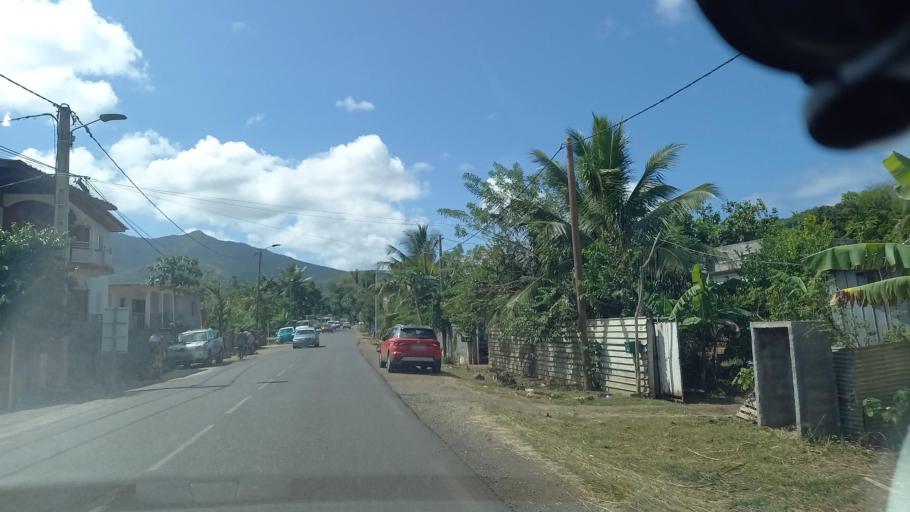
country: YT
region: Chirongui
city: Chirongui
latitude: -12.9220
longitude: 45.1578
